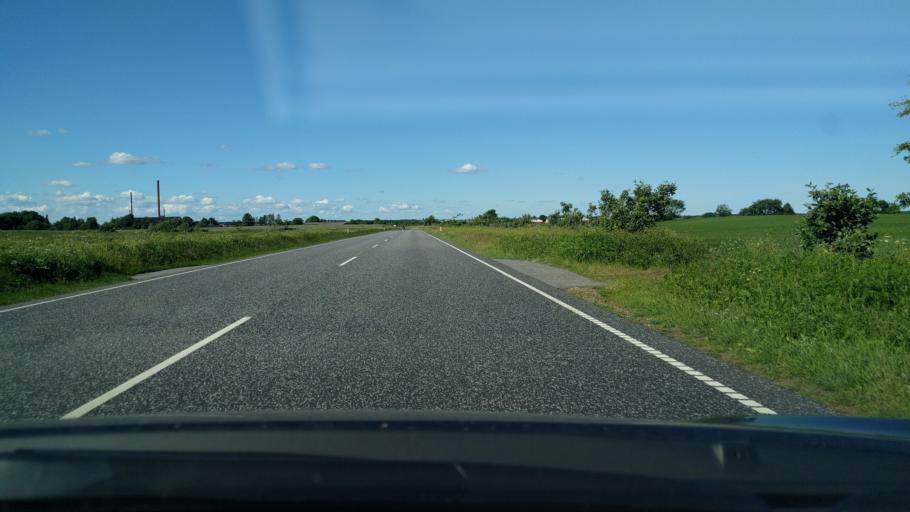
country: DK
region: North Denmark
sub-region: Vesthimmerland Kommune
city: Alestrup
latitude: 56.6084
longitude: 9.5046
